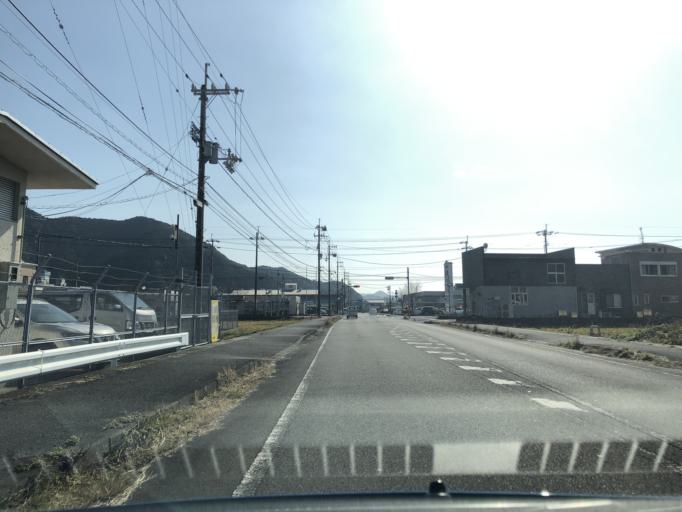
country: JP
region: Kochi
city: Sukumo
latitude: 32.9307
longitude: 132.7079
